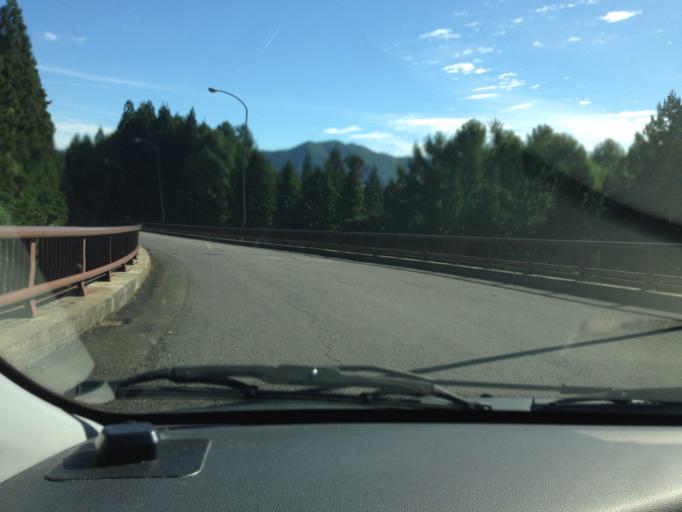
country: JP
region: Fukushima
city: Inawashiro
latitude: 37.5802
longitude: 140.1030
